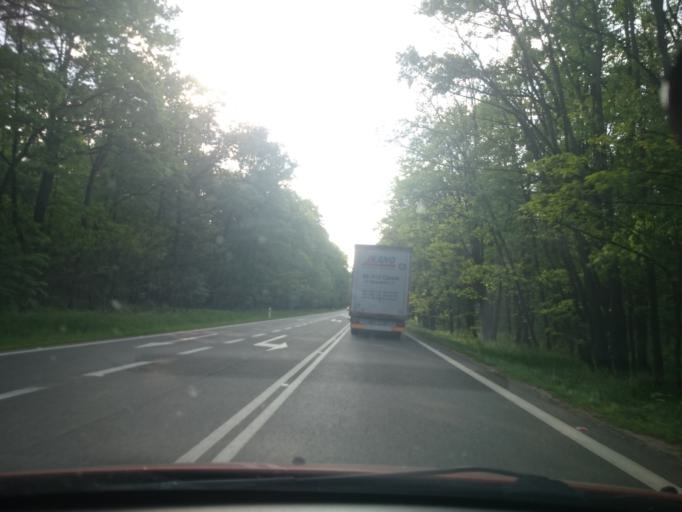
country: PL
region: Opole Voivodeship
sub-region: Powiat opolski
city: Chrzastowice
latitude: 50.6255
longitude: 18.0428
